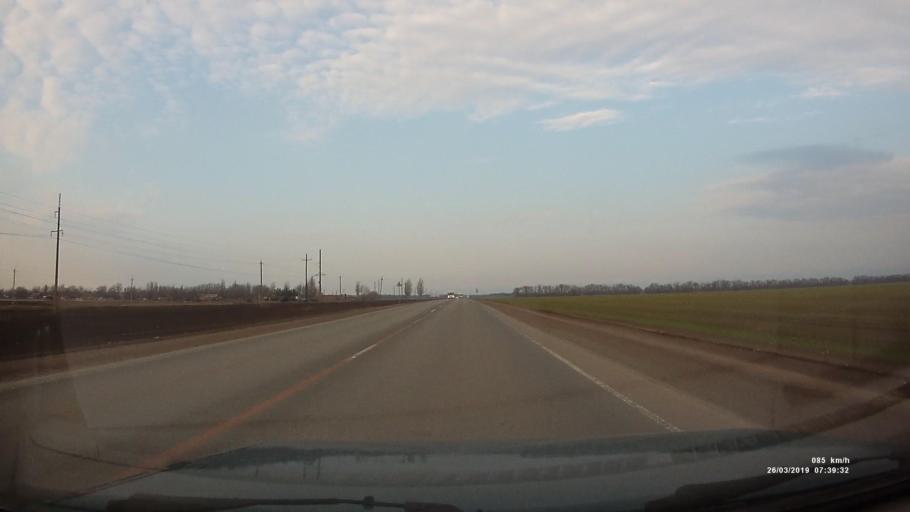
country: RU
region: Rostov
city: Novobessergenovka
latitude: 47.1970
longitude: 38.6636
